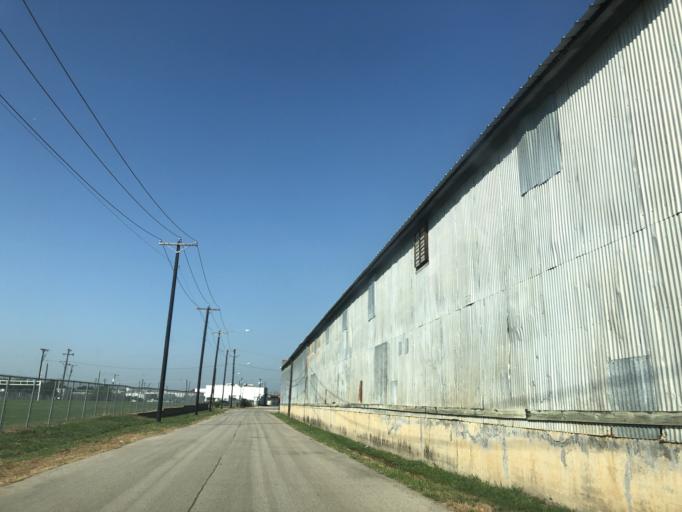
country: US
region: Texas
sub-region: Dallas County
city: Dallas
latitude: 32.7723
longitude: -96.7739
